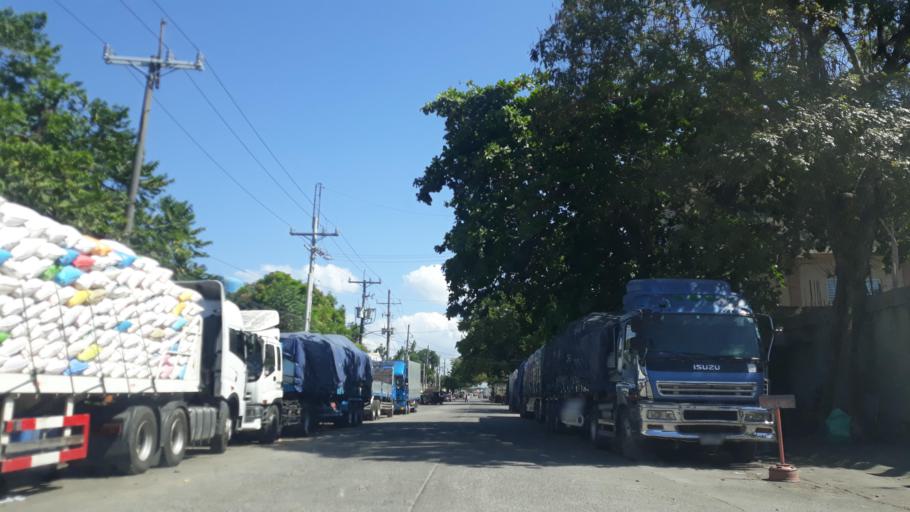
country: PH
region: Calabarzon
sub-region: Province of Cavite
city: Manggahan
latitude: 14.2966
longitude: 120.9176
